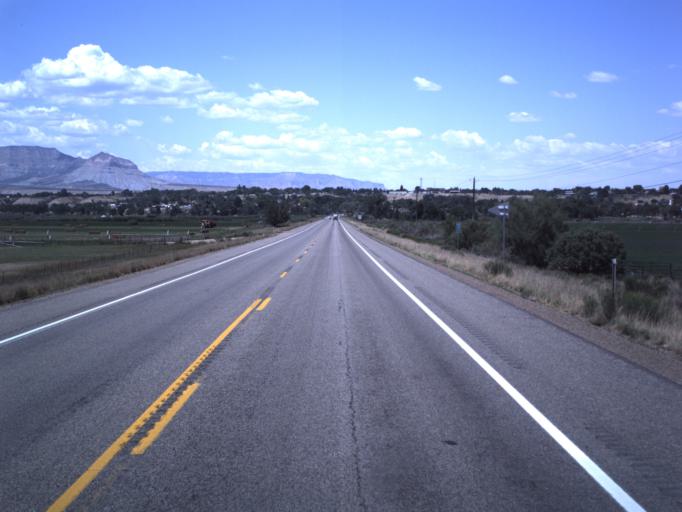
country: US
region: Utah
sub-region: Emery County
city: Castle Dale
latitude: 39.2013
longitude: -111.0242
